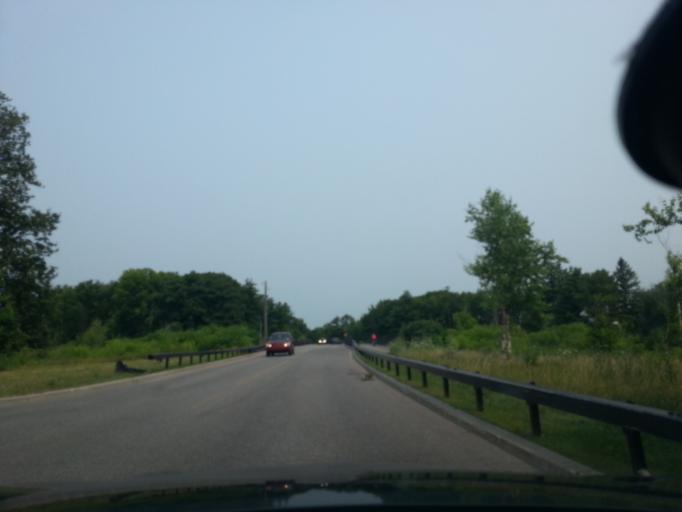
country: CA
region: Ontario
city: Ottawa
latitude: 45.4316
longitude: -75.7498
